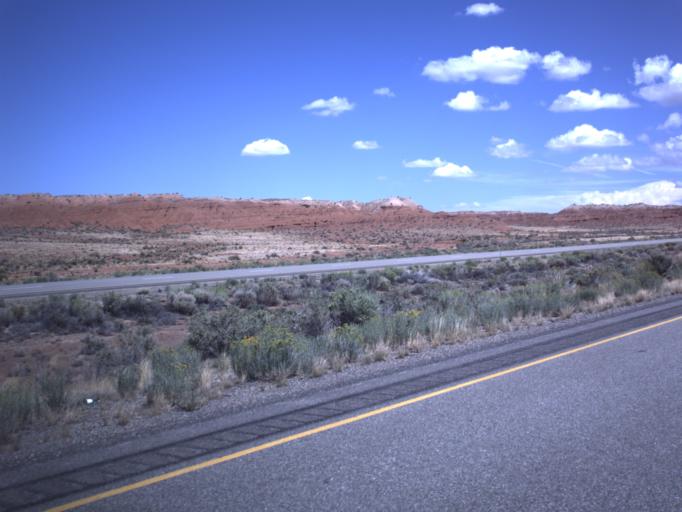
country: US
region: Utah
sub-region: Emery County
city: Ferron
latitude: 38.8461
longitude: -111.0399
